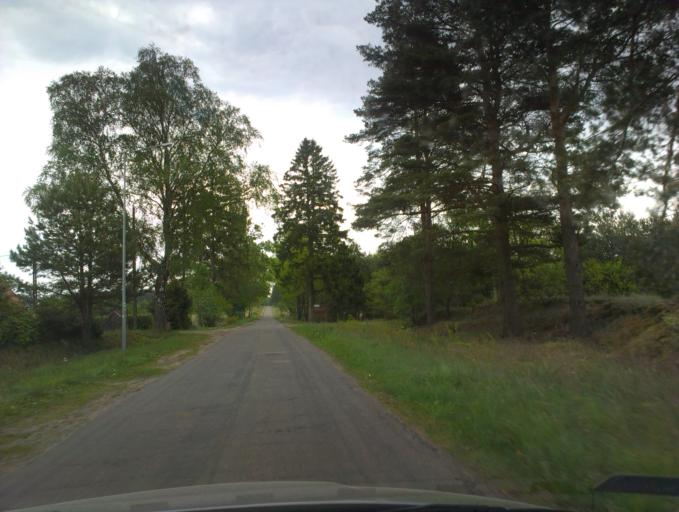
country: PL
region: West Pomeranian Voivodeship
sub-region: Powiat szczecinecki
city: Szczecinek
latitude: 53.8017
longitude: 16.6668
